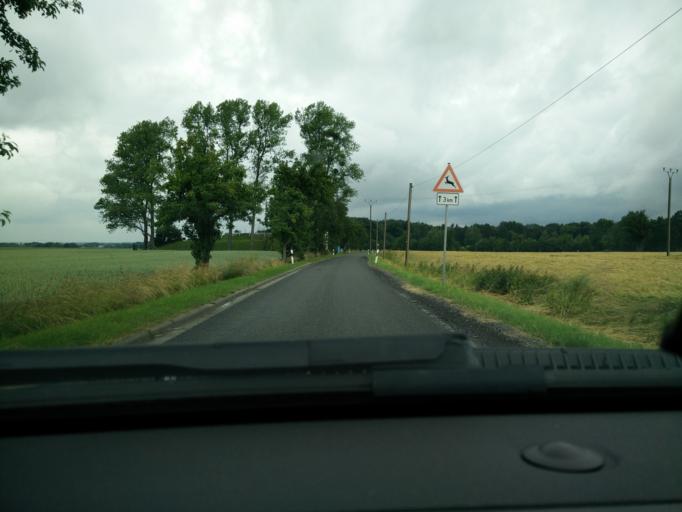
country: DE
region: Saxony
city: Geithain
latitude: 51.1098
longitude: 12.6897
